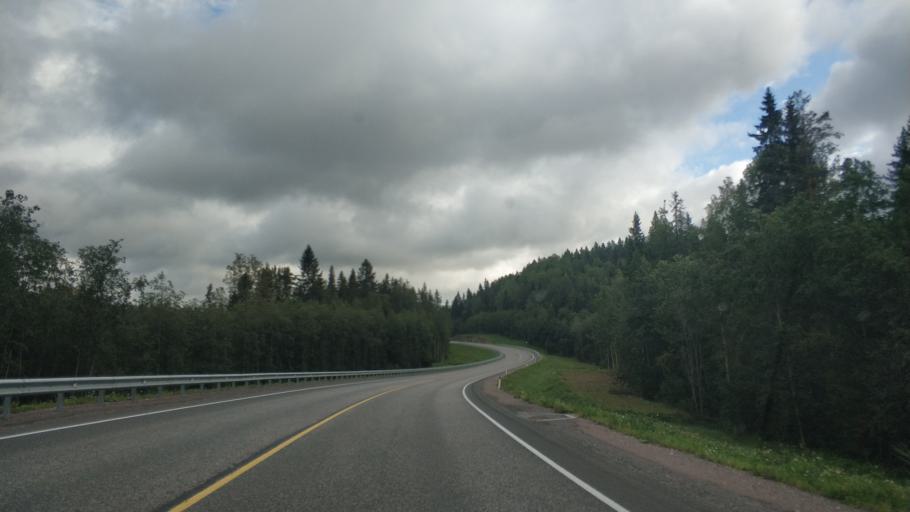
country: RU
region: Republic of Karelia
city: Khelyulya
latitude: 61.8308
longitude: 30.6360
